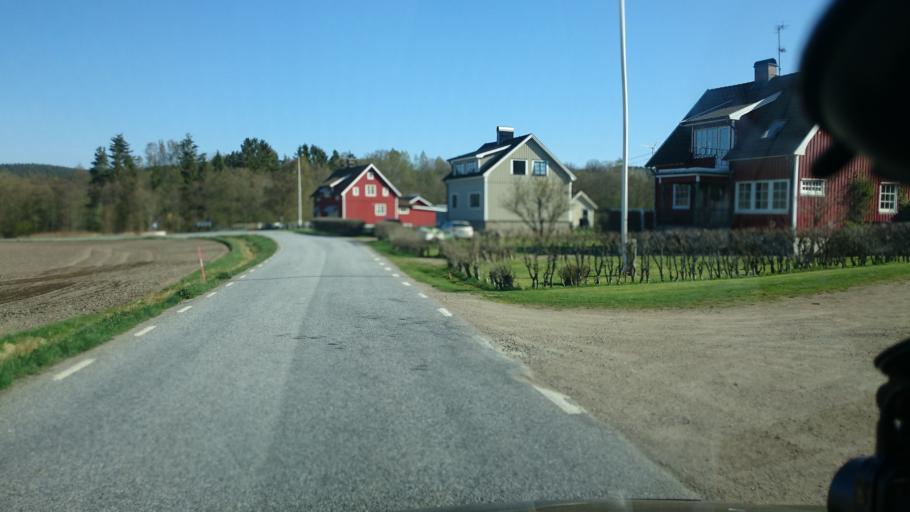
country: SE
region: Vaestra Goetaland
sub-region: Munkedals Kommun
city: Munkedal
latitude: 58.3880
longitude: 11.6630
